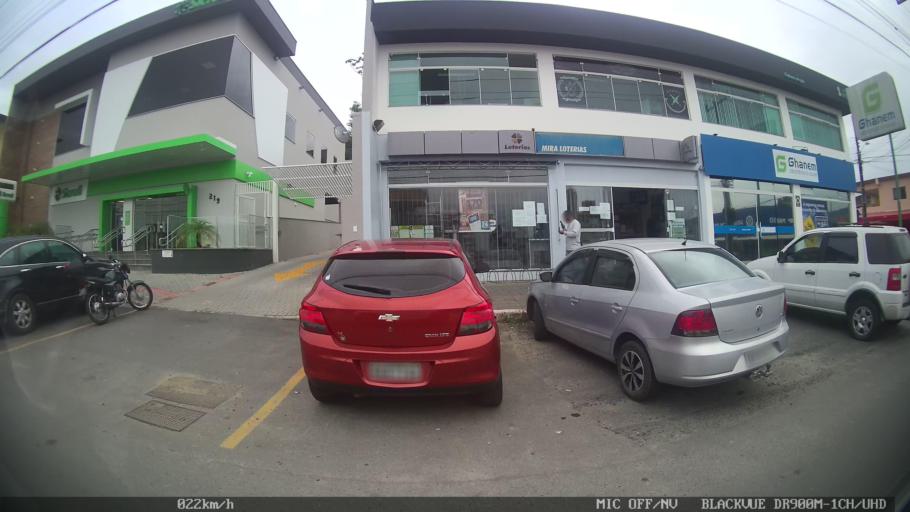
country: BR
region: Santa Catarina
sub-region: Joinville
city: Joinville
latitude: -26.2715
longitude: -48.8722
